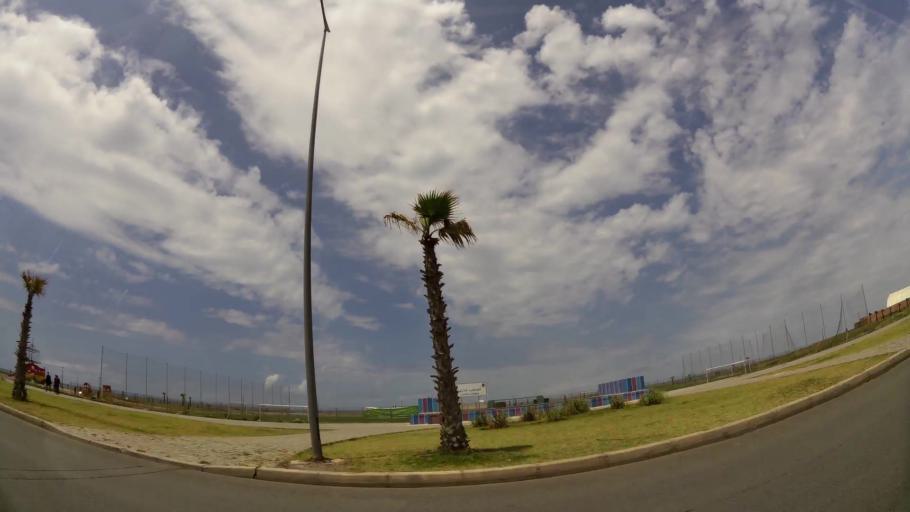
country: MA
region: Rabat-Sale-Zemmour-Zaer
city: Sale
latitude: 34.0602
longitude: -6.8149
